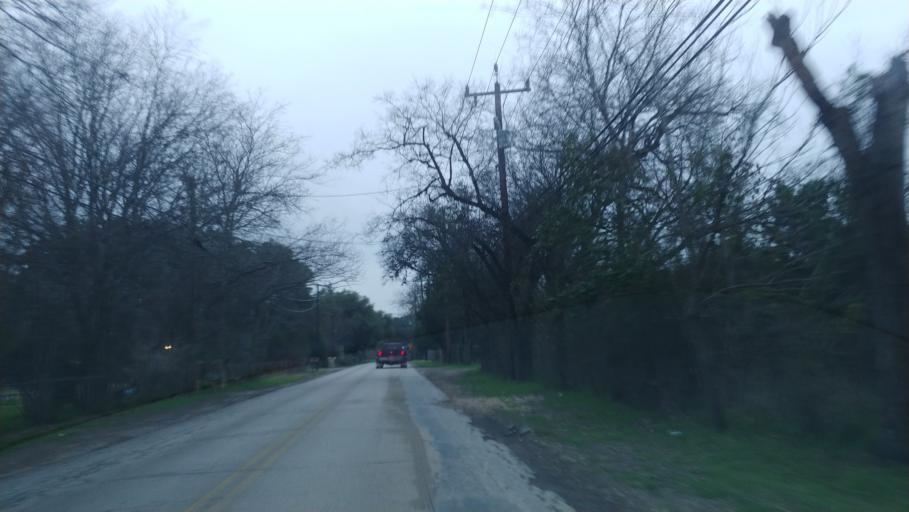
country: US
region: Texas
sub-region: Bexar County
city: Helotes
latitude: 29.6108
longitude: -98.6848
